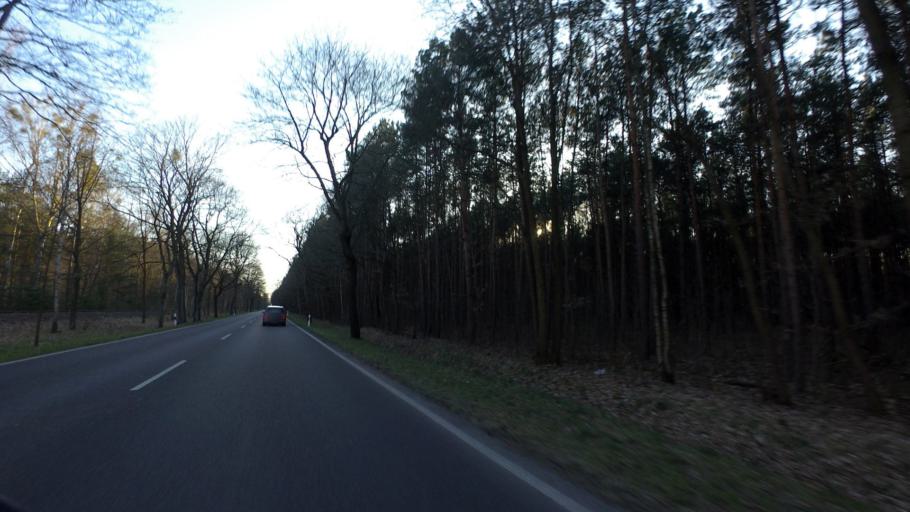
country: DE
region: Brandenburg
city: Werftpfuhl
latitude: 52.6677
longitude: 13.8102
